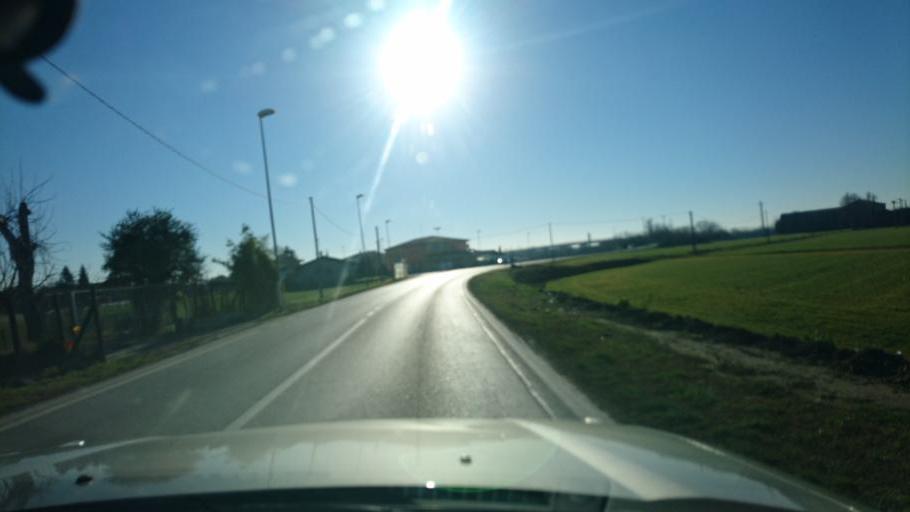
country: IT
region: Veneto
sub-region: Provincia di Rovigo
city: Loreo
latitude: 45.0525
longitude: 12.2055
